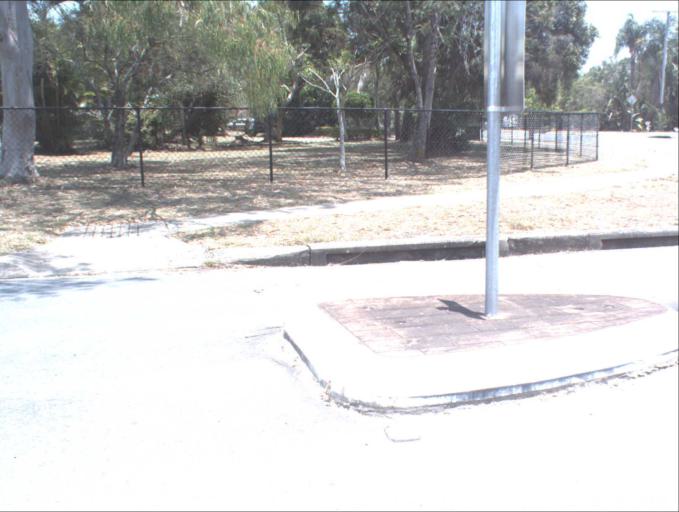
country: AU
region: Queensland
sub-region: Logan
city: Slacks Creek
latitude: -27.6660
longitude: 153.1833
